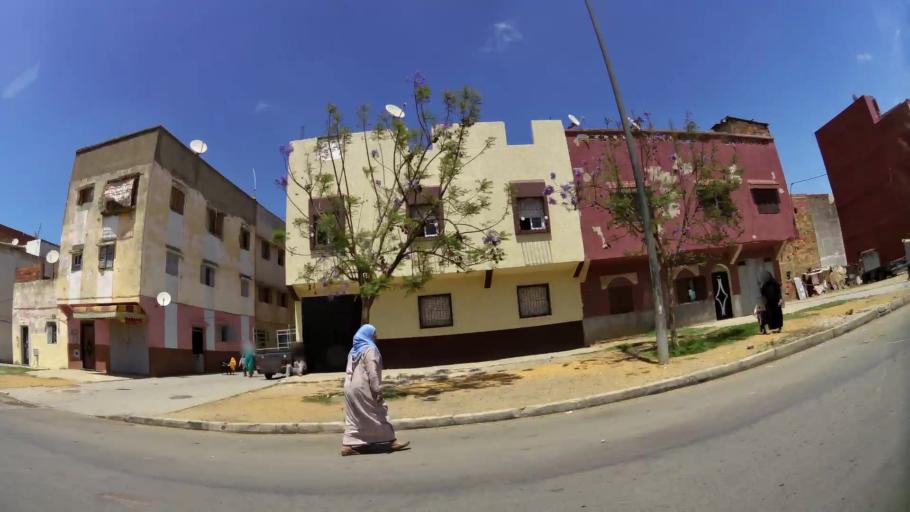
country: MA
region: Gharb-Chrarda-Beni Hssen
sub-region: Kenitra Province
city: Kenitra
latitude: 34.2571
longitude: -6.5481
